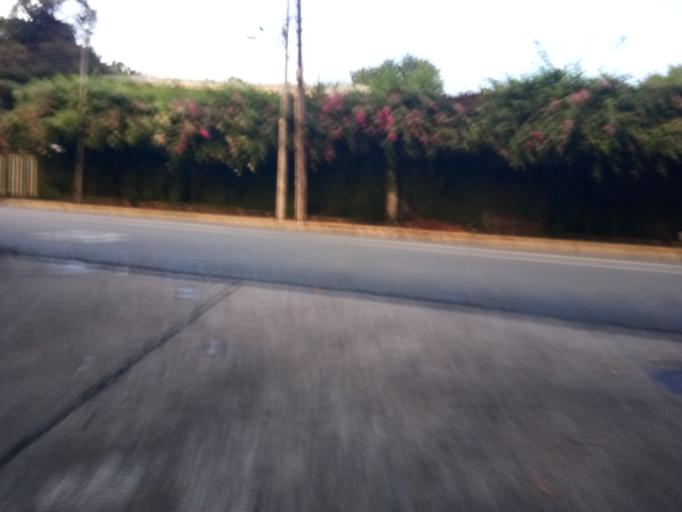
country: PH
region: Metro Manila
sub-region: San Juan
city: San Juan
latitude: 14.6162
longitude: 121.0427
